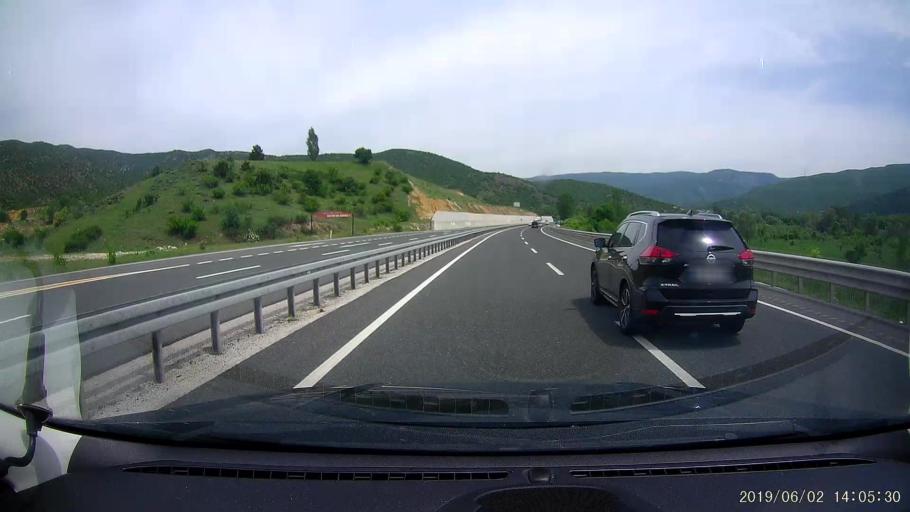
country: TR
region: Cankiri
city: Ilgaz
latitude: 40.9009
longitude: 33.6698
